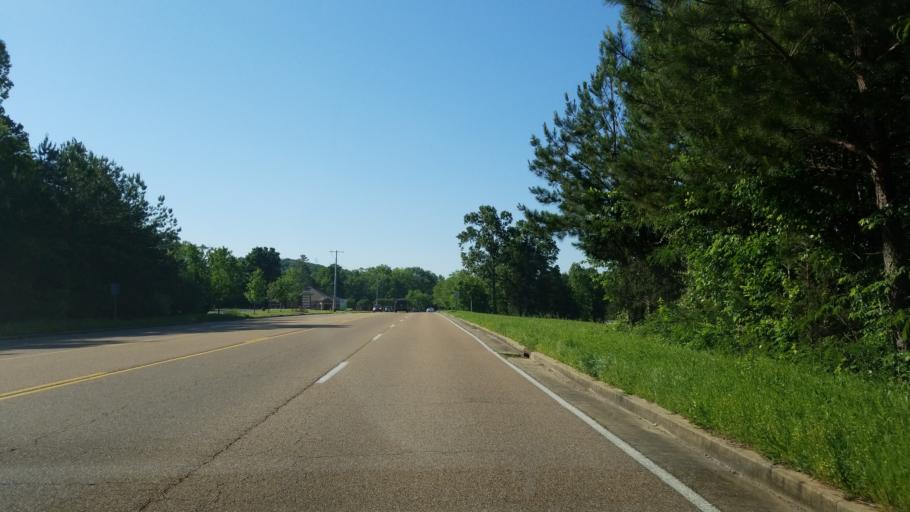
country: US
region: Tennessee
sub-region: Hamilton County
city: East Brainerd
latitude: 35.0489
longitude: -85.1289
